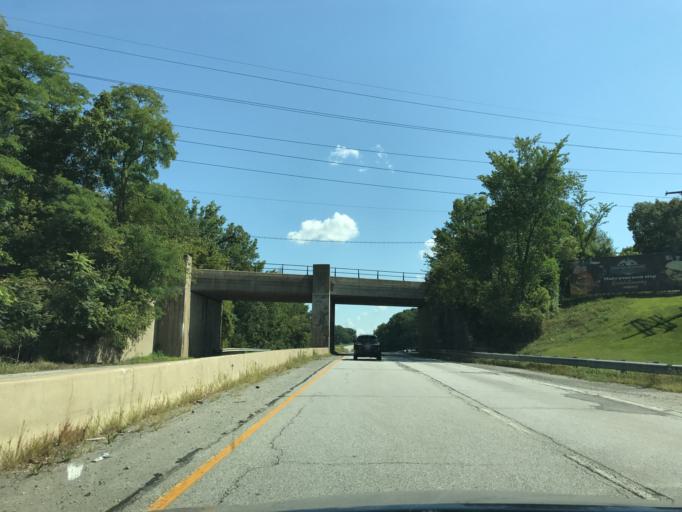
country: US
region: Indiana
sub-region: Porter County
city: Valparaiso
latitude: 41.4576
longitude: -87.0509
